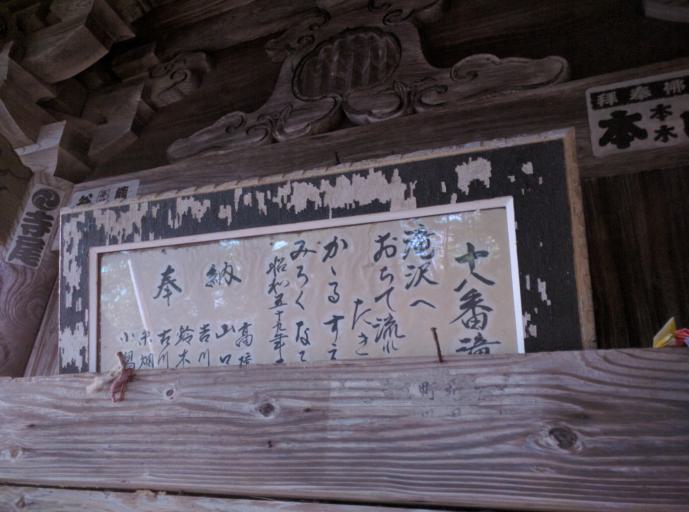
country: JP
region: Fukushima
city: Kitakata
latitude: 37.5097
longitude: 139.9441
